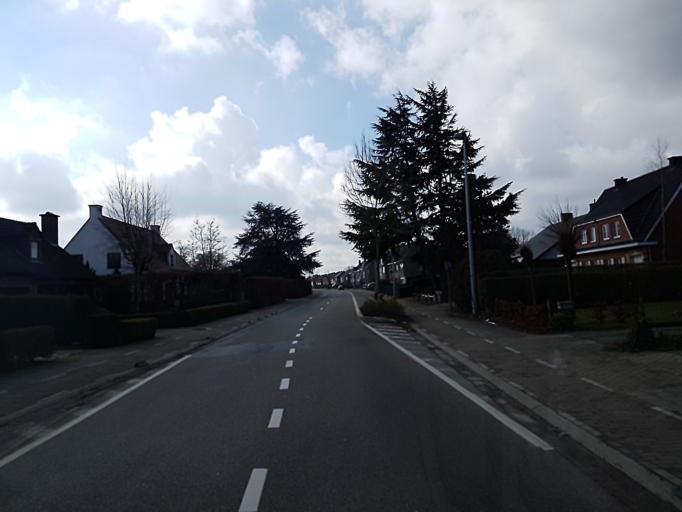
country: BE
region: Flanders
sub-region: Provincie Oost-Vlaanderen
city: Sint-Niklaas
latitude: 51.1705
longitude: 4.1126
